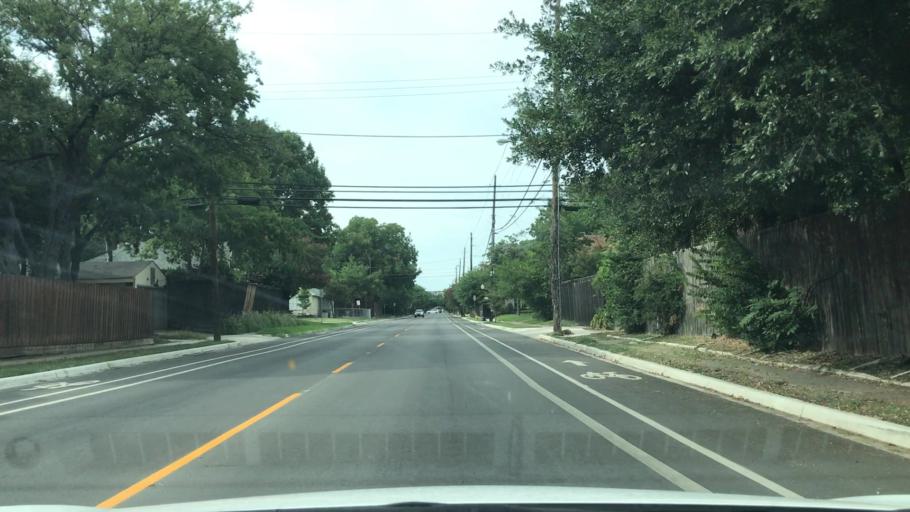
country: US
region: Texas
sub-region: Dallas County
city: Highland Park
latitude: 32.8236
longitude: -96.7747
